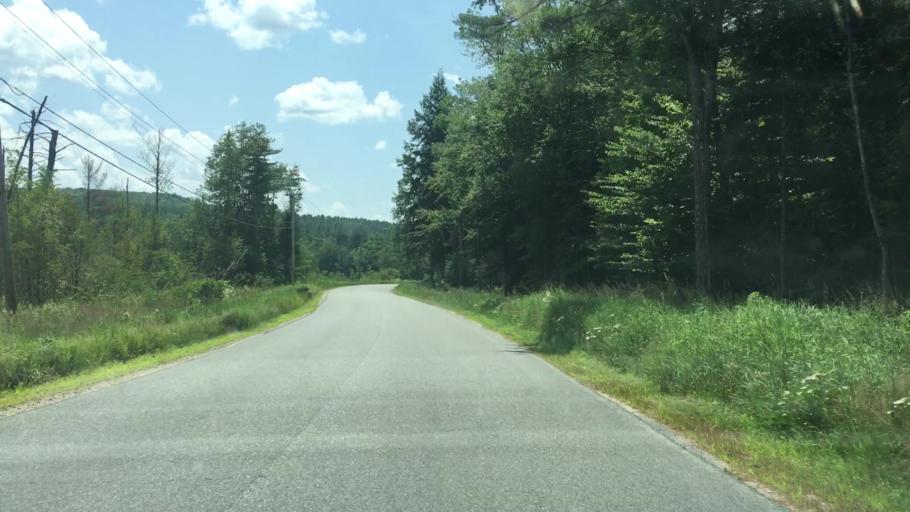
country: US
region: New Hampshire
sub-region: Grafton County
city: Enfield
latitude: 43.6819
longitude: -72.0935
